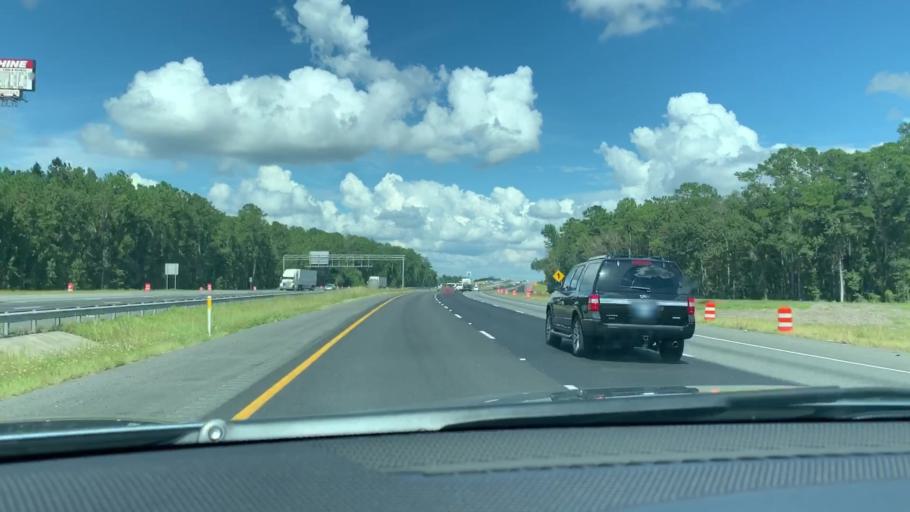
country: US
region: Georgia
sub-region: Camden County
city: Woodbine
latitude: 30.9476
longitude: -81.6860
